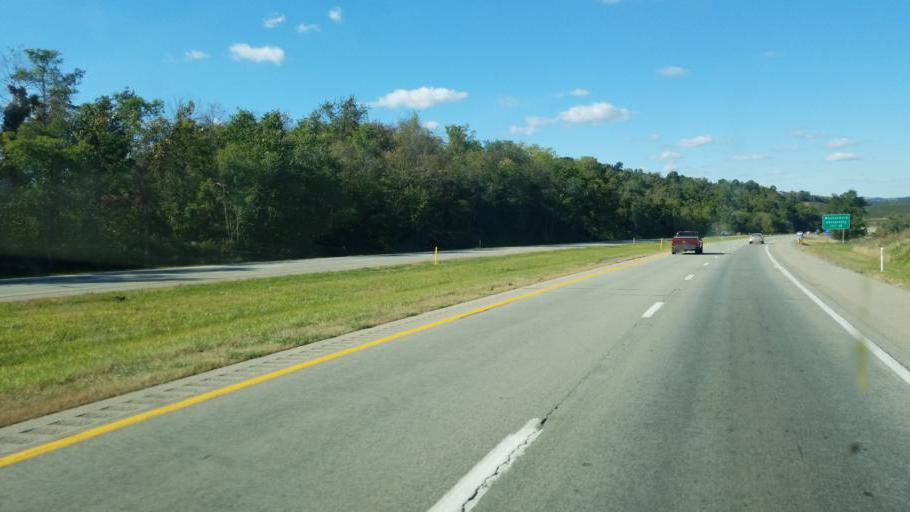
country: US
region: Pennsylvania
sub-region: Greene County
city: Morrisville
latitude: 39.8769
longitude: -80.1329
